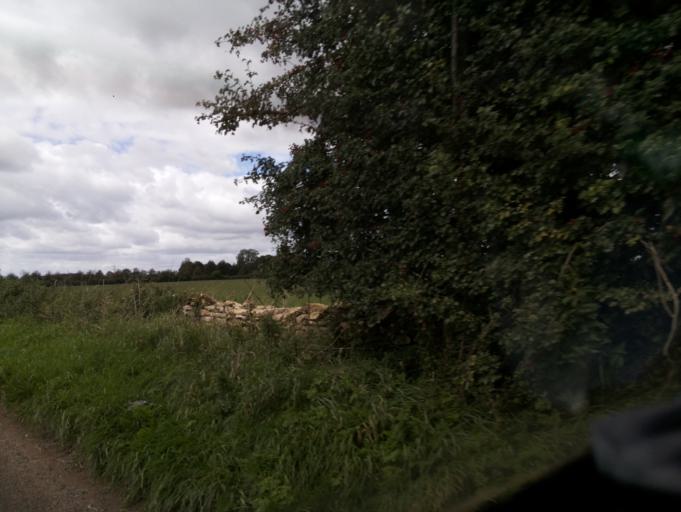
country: GB
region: England
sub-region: South Gloucestershire
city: Marshfield
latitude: 51.4926
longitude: -2.3035
